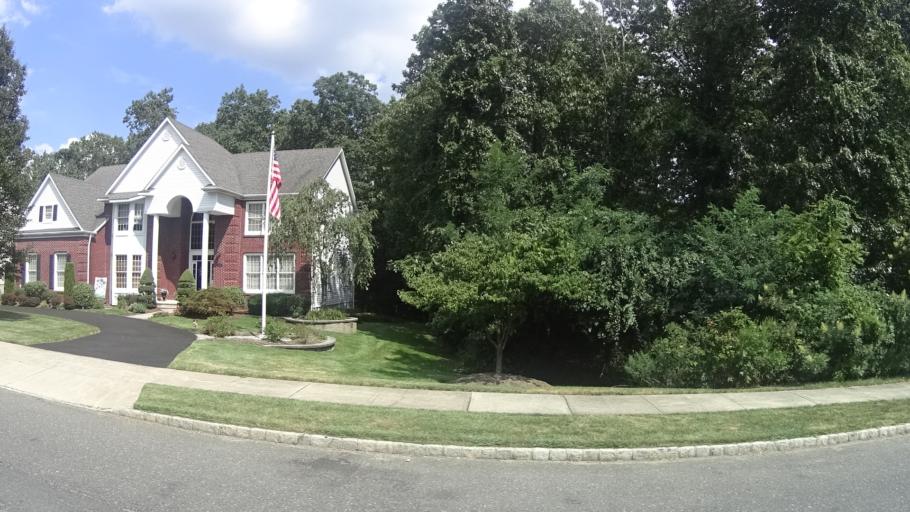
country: US
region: New Jersey
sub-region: Monmouth County
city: Brielle
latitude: 40.1200
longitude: -74.0864
